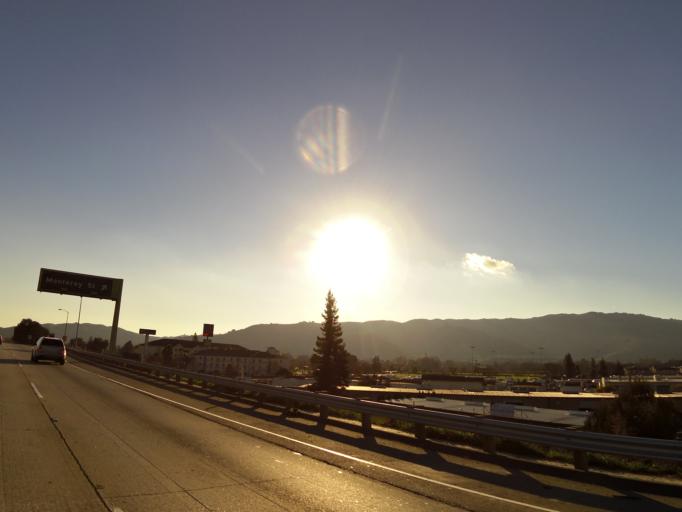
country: US
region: California
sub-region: Santa Clara County
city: Gilroy
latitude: 36.9912
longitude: -121.5579
